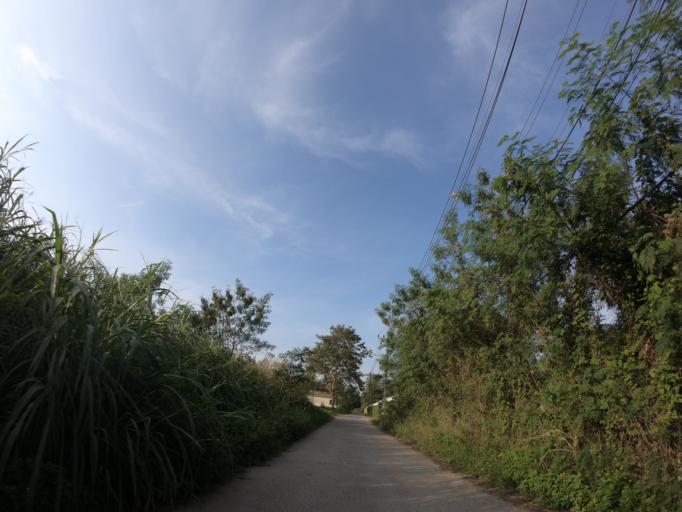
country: TH
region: Chiang Mai
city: Chiang Mai
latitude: 18.8316
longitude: 98.9819
